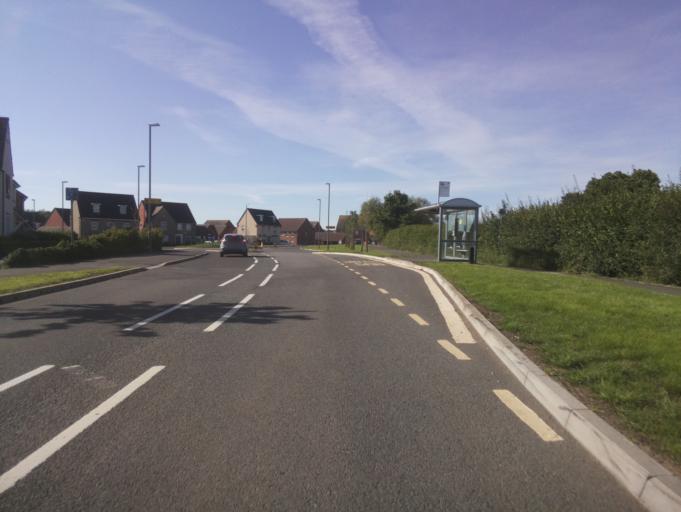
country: GB
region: England
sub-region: Bath and North East Somerset
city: Keynsham
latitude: 51.4043
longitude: -2.5165
